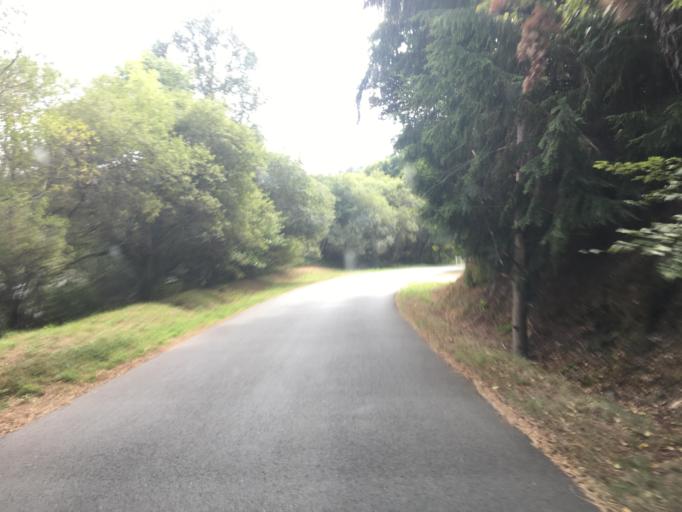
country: FR
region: Brittany
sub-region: Departement des Cotes-d'Armor
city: Gouarec
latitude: 48.2074
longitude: -3.1162
